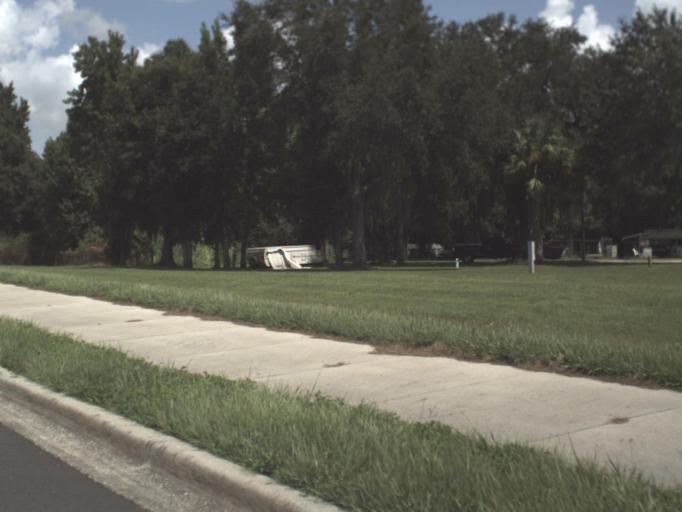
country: US
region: Florida
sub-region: Hardee County
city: Zolfo Springs
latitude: 27.5088
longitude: -81.8028
